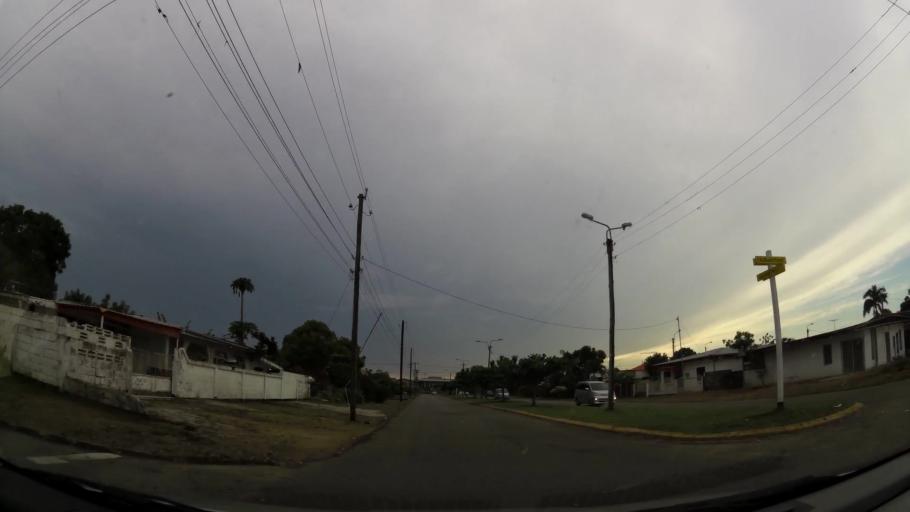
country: SR
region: Paramaribo
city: Paramaribo
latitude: 5.8105
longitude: -55.2031
